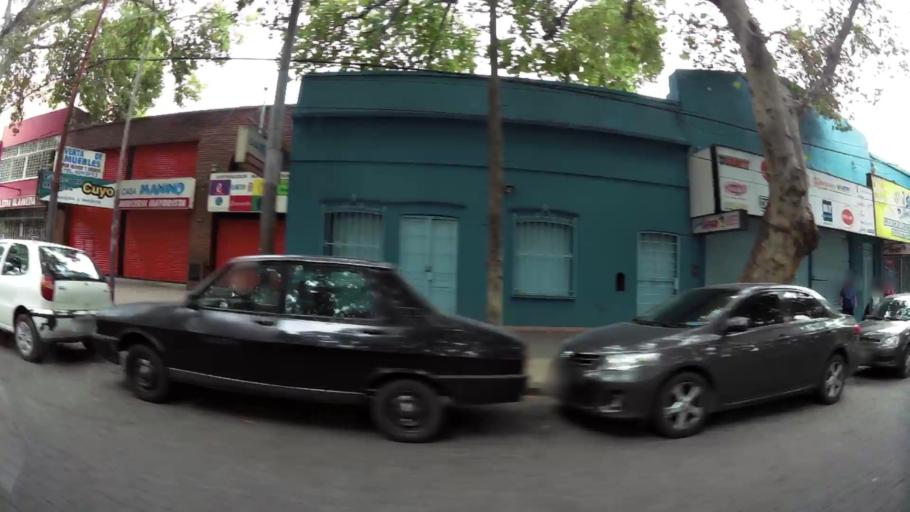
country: AR
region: Mendoza
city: Mendoza
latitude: -32.8803
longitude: -68.8368
